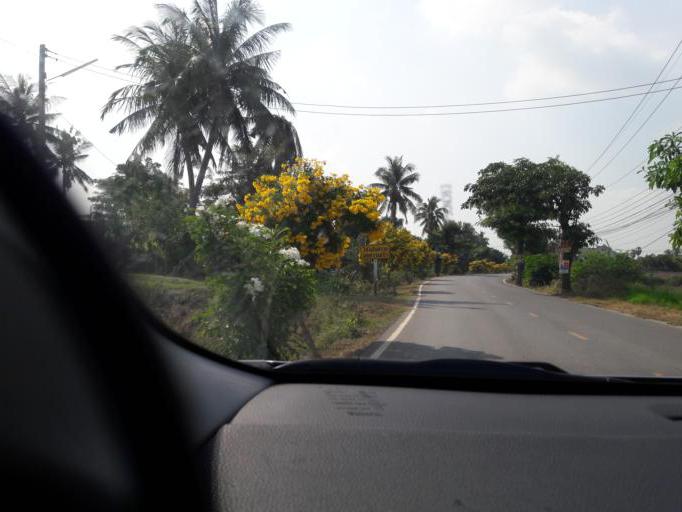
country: TH
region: Ang Thong
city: Pa Mok
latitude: 14.5341
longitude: 100.3877
